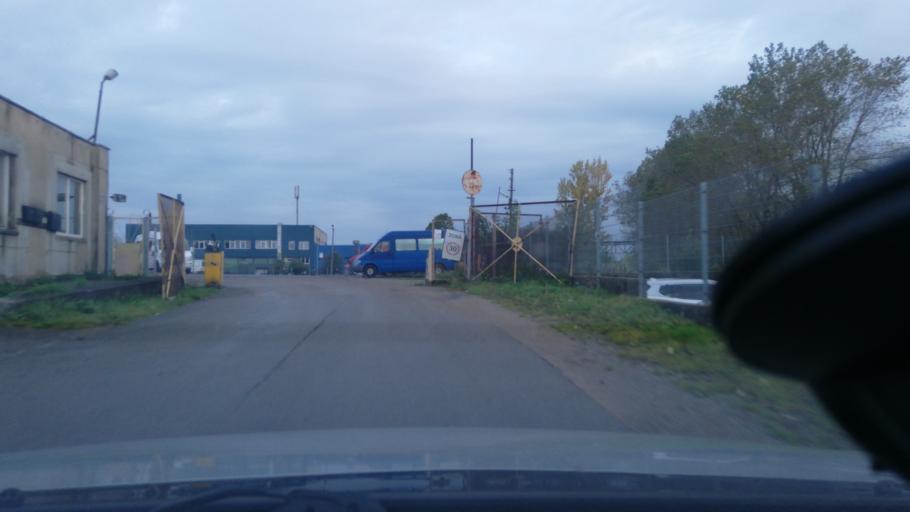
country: LT
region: Klaipedos apskritis
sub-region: Klaipeda
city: Klaipeda
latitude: 55.6873
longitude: 21.1852
